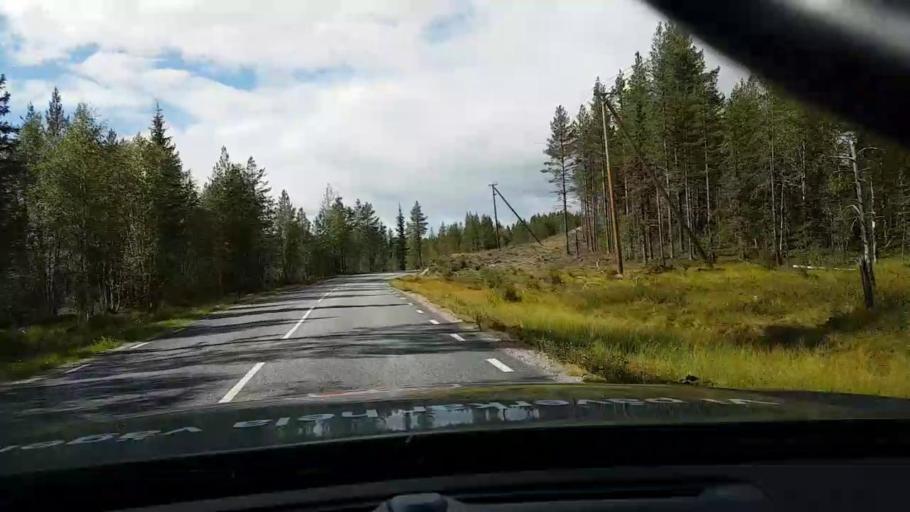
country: SE
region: Vaesterbotten
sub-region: Asele Kommun
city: Asele
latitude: 63.8482
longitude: 17.4063
